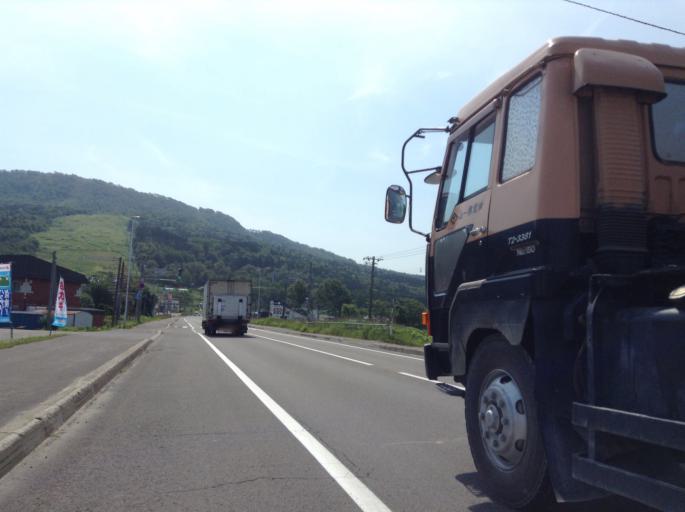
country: JP
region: Hokkaido
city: Nayoro
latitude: 44.7246
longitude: 142.2651
